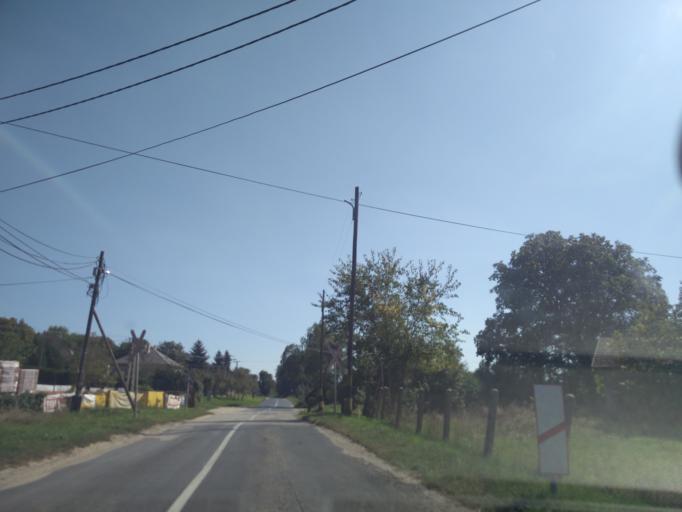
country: HU
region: Fejer
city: Lovasbereny
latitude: 47.3053
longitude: 18.5594
